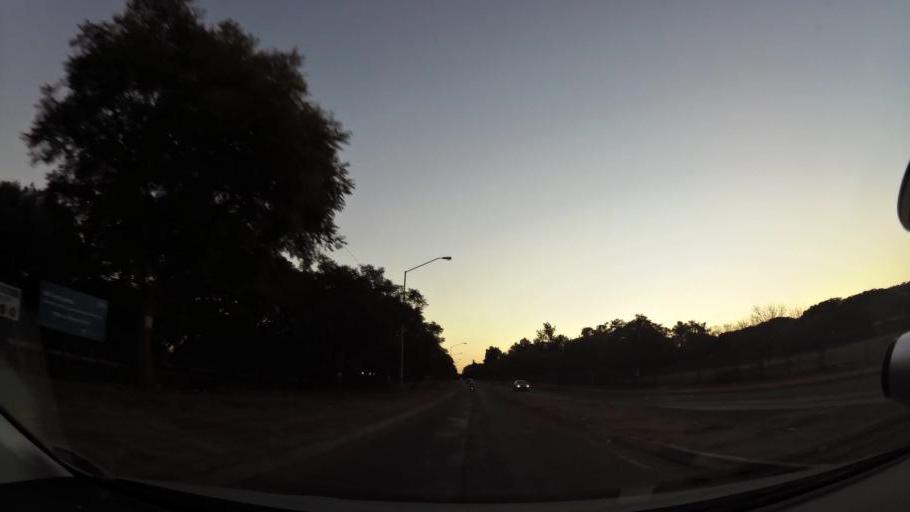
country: ZA
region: Gauteng
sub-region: City of Tshwane Metropolitan Municipality
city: Pretoria
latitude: -25.7389
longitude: 28.1589
